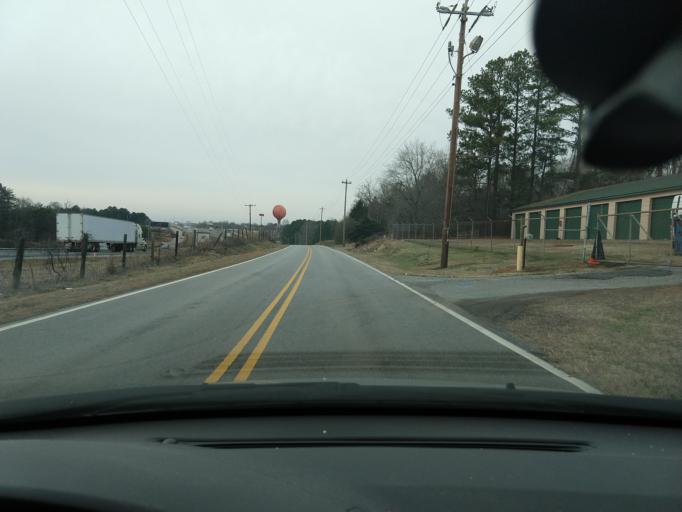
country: US
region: South Carolina
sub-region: Cherokee County
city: Gaffney
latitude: 35.0974
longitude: -81.6775
